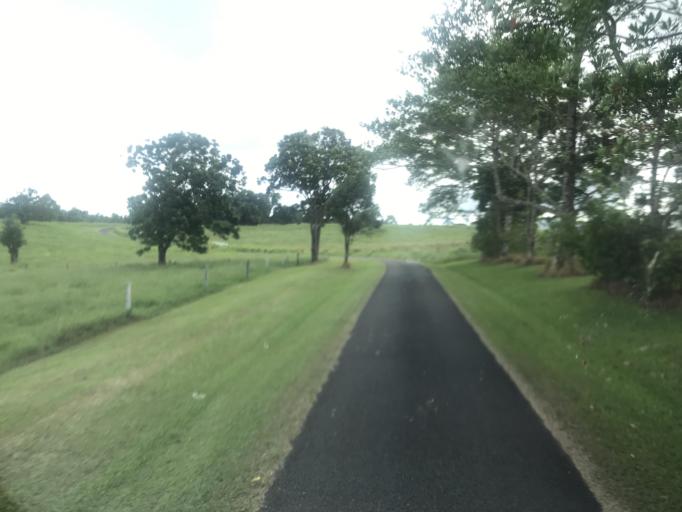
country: AU
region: Queensland
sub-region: Tablelands
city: Ravenshoe
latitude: -17.5551
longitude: 145.6911
